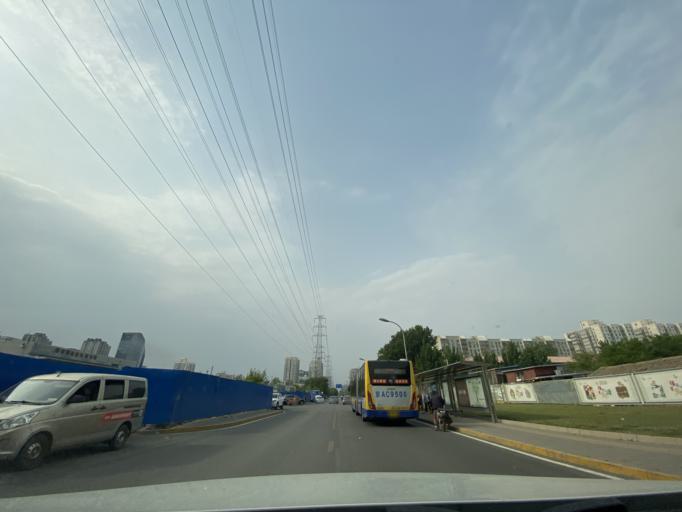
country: CN
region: Beijing
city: Haidian
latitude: 39.9824
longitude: 116.3346
